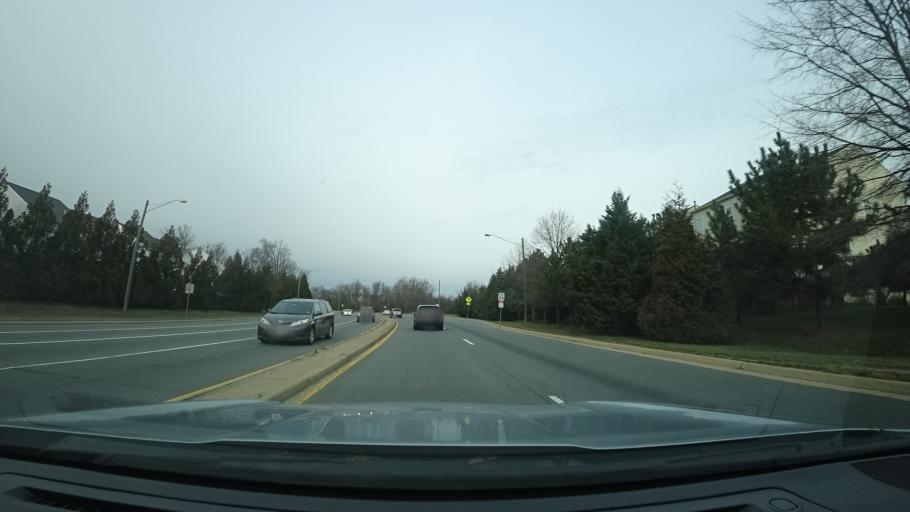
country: US
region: Virginia
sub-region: Fairfax County
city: Floris
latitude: 38.9454
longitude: -77.3935
